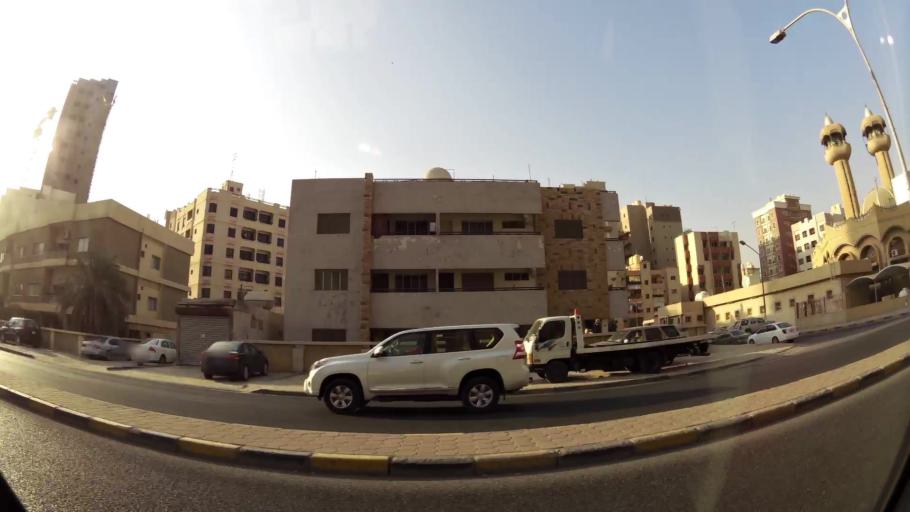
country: KW
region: Muhafazat Hawalli
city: Hawalli
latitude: 29.3366
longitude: 48.0521
